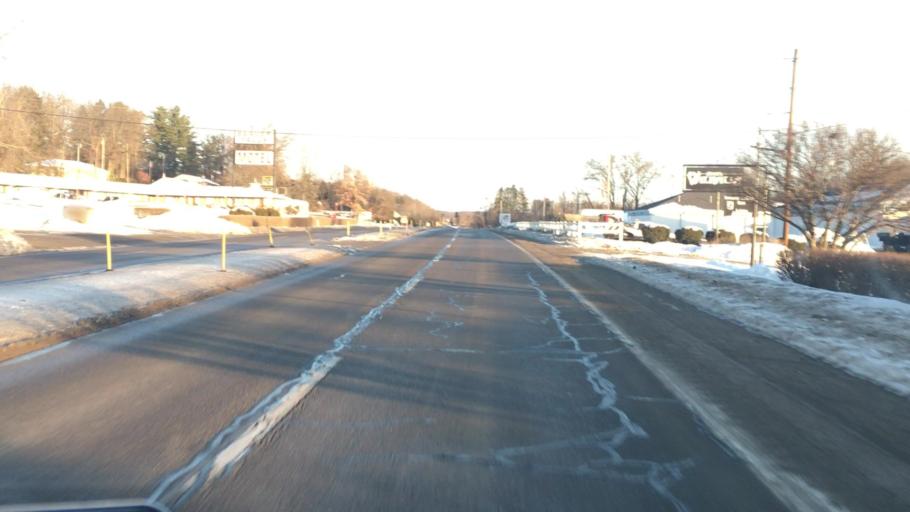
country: US
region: Pennsylvania
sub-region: Beaver County
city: Big Beaver
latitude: 40.8221
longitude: -80.3243
